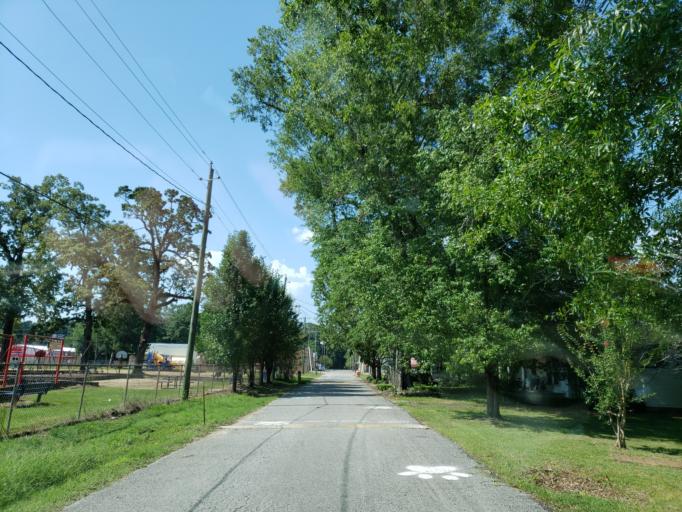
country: US
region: Mississippi
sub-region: Covington County
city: Collins
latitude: 31.5605
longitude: -89.4987
